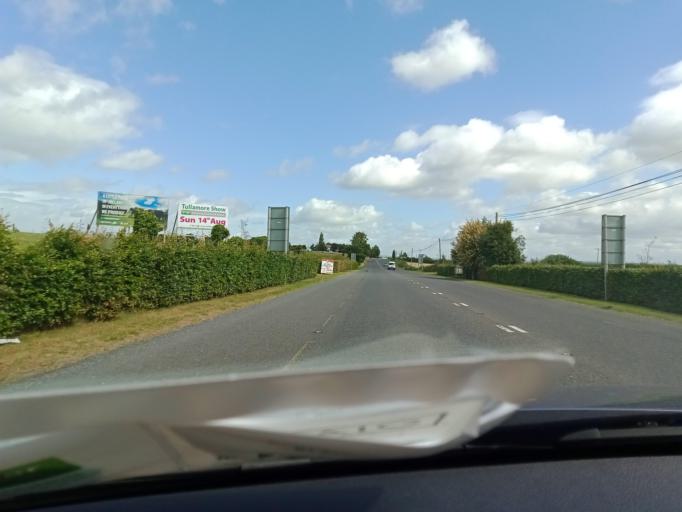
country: IE
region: Leinster
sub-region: Laois
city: Rathdowney
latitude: 52.8217
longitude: -7.4703
